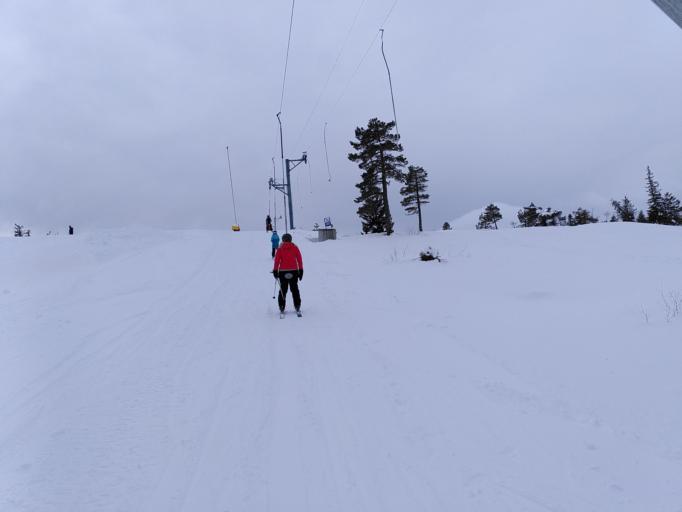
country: NO
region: Buskerud
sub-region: Flesberg
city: Lampeland
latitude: 59.8012
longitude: 9.3911
